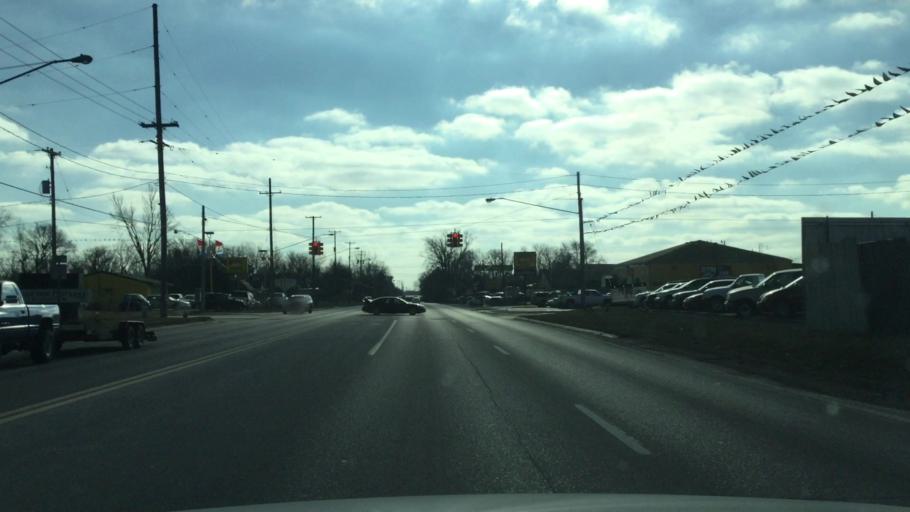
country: US
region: Michigan
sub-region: Genesee County
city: Beecher
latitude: 43.0692
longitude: -83.6741
